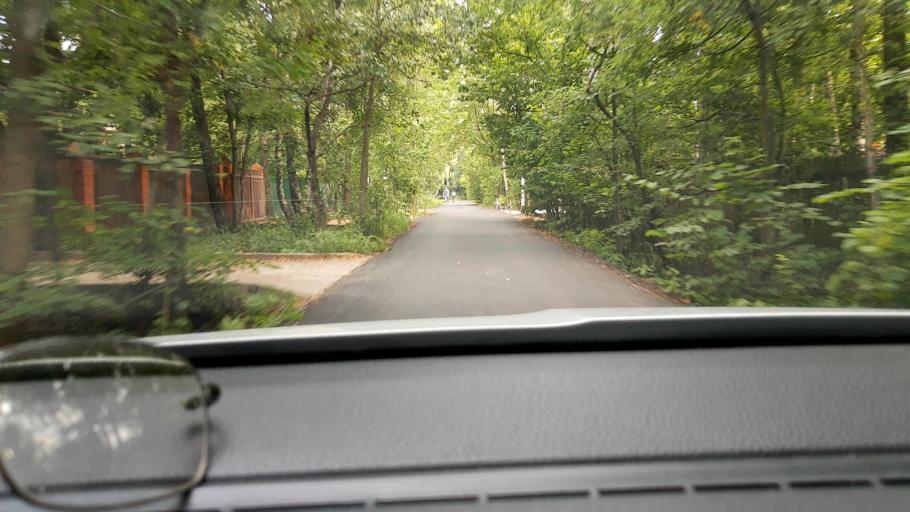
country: RU
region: Moskovskaya
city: Kokoshkino
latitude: 55.5940
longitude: 37.1624
